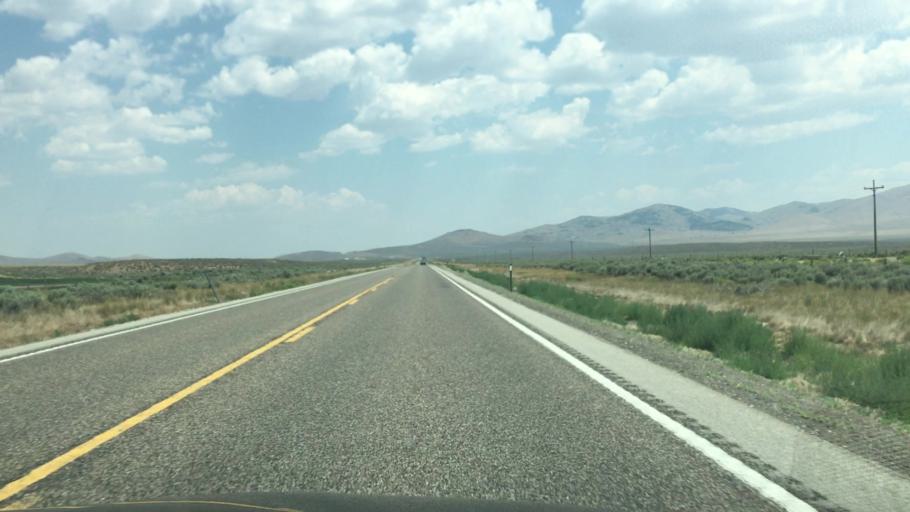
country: US
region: Nevada
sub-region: Elko County
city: Wells
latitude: 41.1456
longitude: -114.9082
